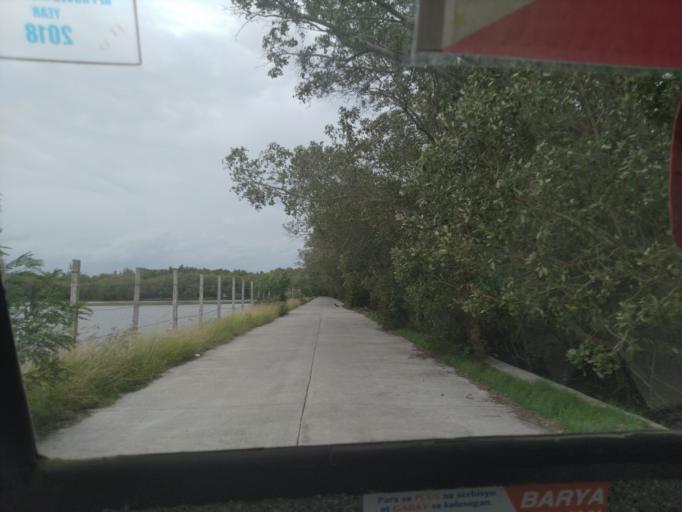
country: PH
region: Central Visayas
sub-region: Province of Negros Oriental
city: Okiot
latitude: 9.5446
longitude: 123.1537
